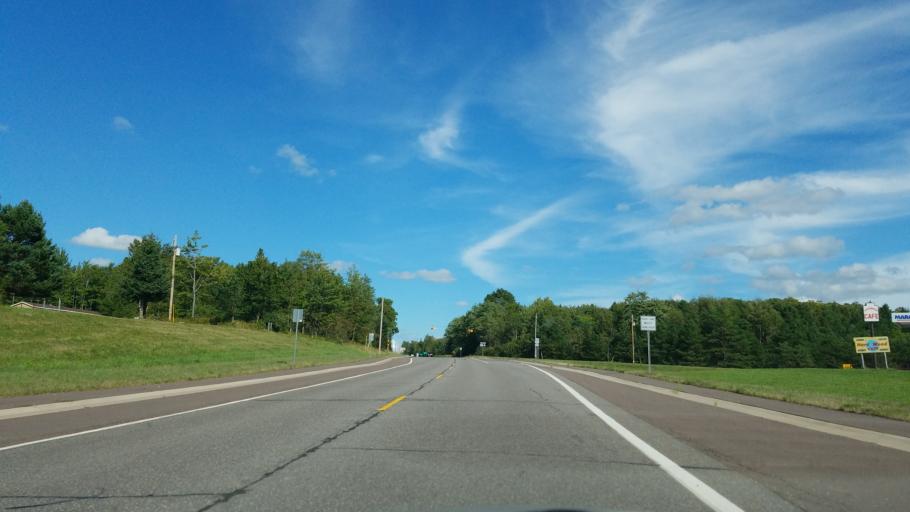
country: US
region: Michigan
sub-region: Baraga County
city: L'Anse
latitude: 46.5462
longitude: -88.5388
